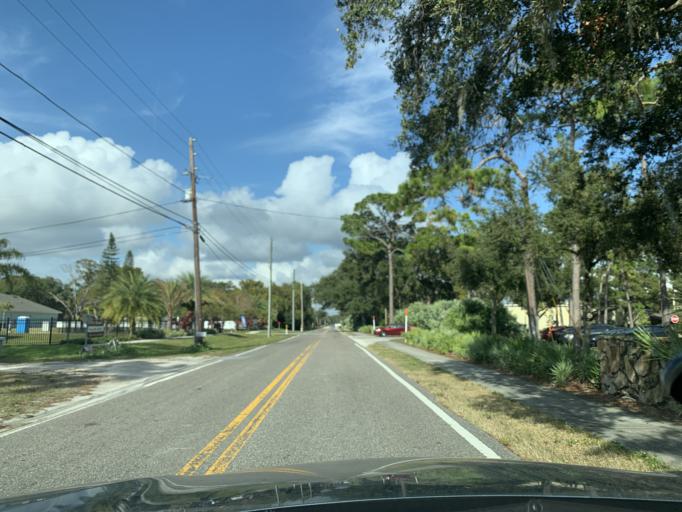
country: US
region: Florida
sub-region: Pinellas County
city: South Highpoint
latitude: 27.9182
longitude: -82.7136
